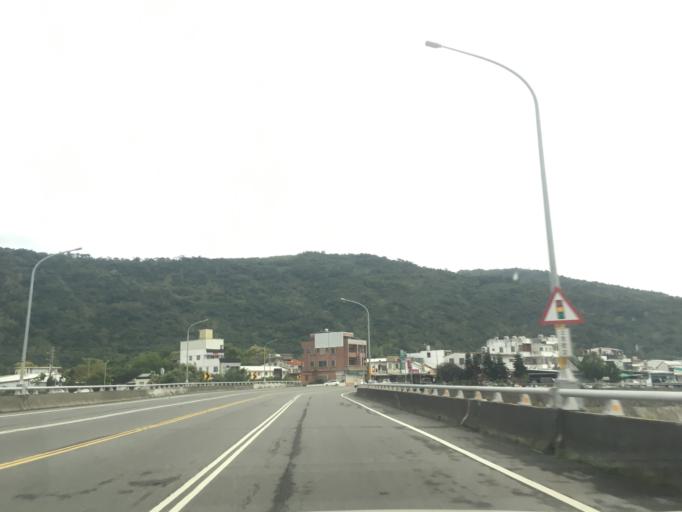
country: TW
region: Taiwan
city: Taitung City
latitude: 22.7608
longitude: 121.0494
